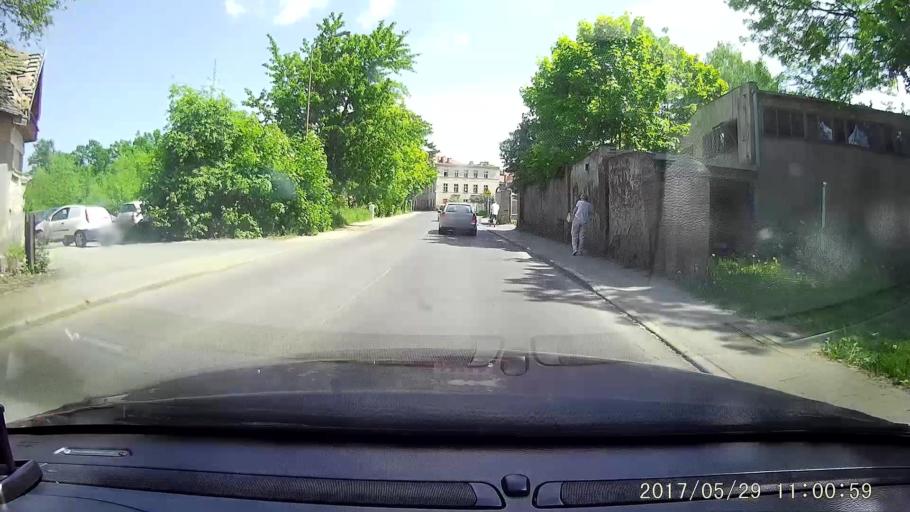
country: PL
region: Lower Silesian Voivodeship
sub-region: Jelenia Gora
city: Jelenia Gora
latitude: 50.9043
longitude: 15.7396
